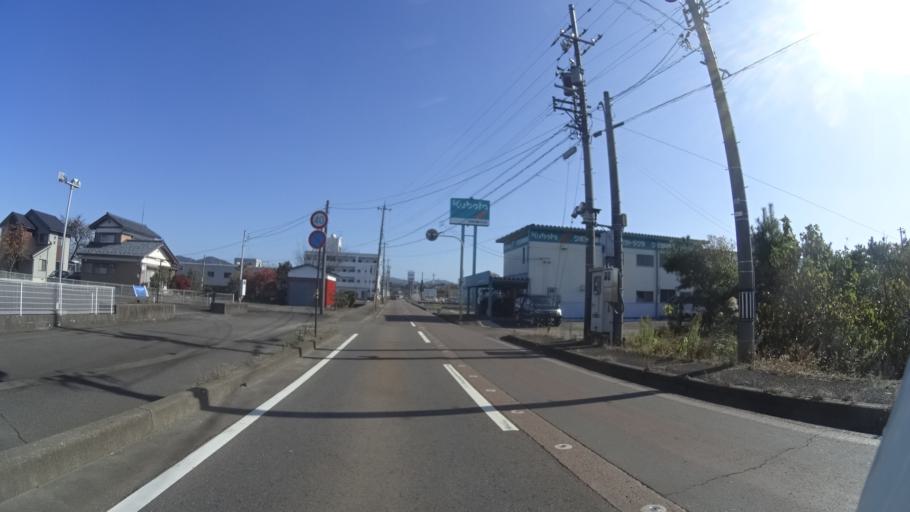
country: JP
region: Fukui
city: Sabae
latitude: 35.9640
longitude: 136.1726
